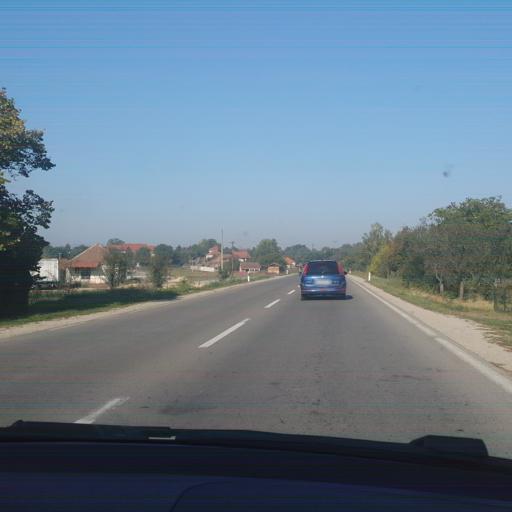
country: RS
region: Central Serbia
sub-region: Toplicki Okrug
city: Prokuplje
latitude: 43.2406
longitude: 21.4909
